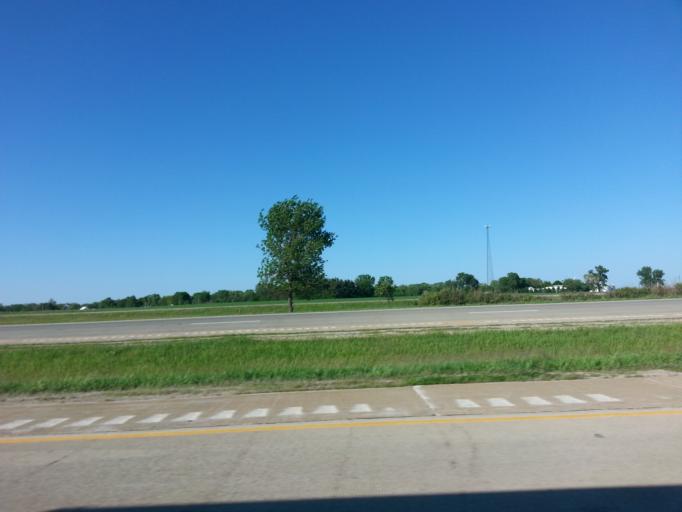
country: US
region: Illinois
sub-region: Woodford County
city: Minonk
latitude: 40.8903
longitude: -89.0403
